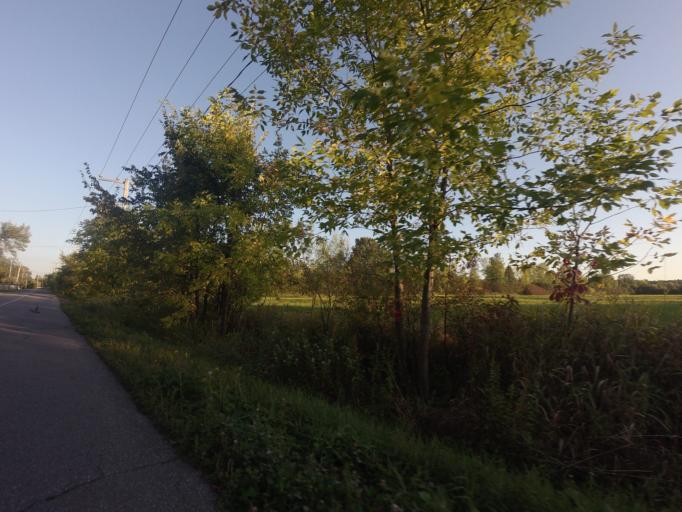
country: CA
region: Quebec
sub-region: Monteregie
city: Hudson
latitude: 45.4763
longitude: -74.1970
